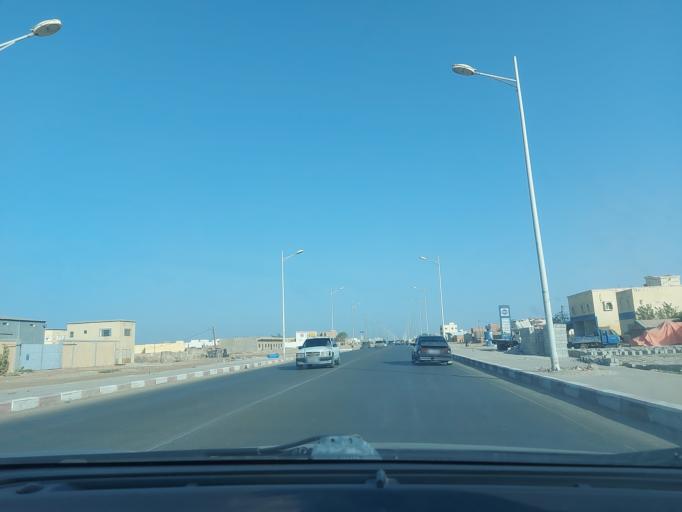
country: MR
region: Nouakchott
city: Nouakchott
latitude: 18.0878
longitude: -16.0048
